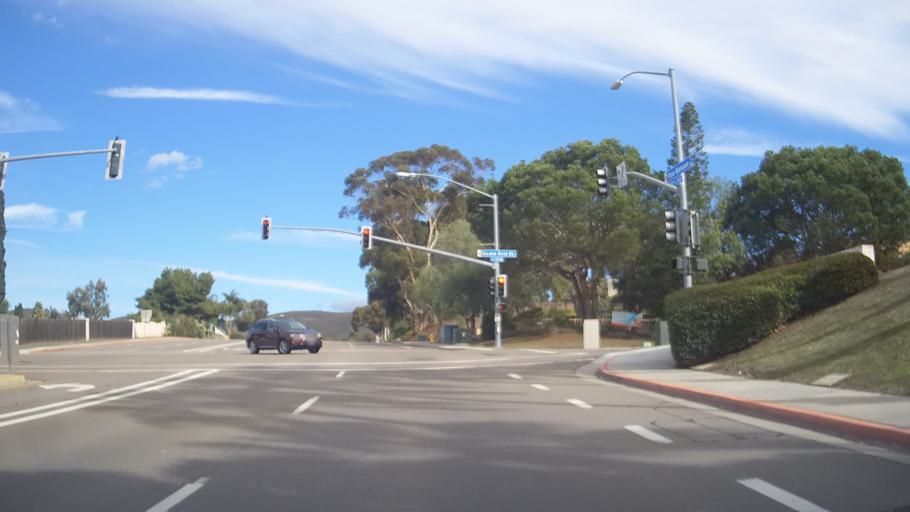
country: US
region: California
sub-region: San Diego County
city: Fairbanks Ranch
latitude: 32.9597
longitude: -117.1231
